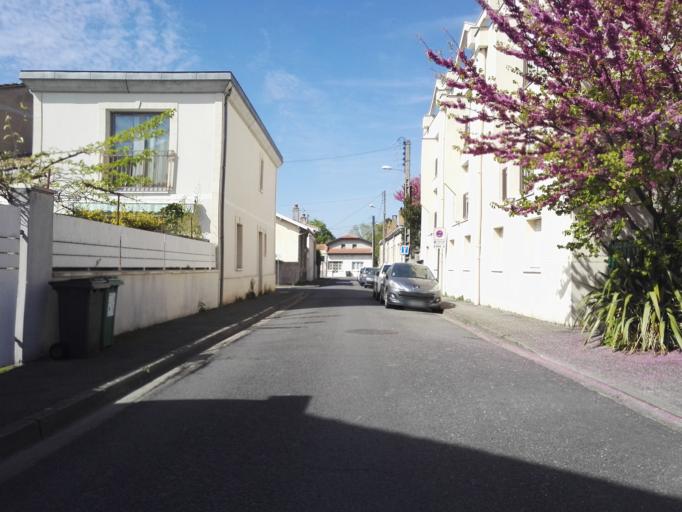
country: FR
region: Aquitaine
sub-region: Departement de la Gironde
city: Talence
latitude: 44.8139
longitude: -0.5841
